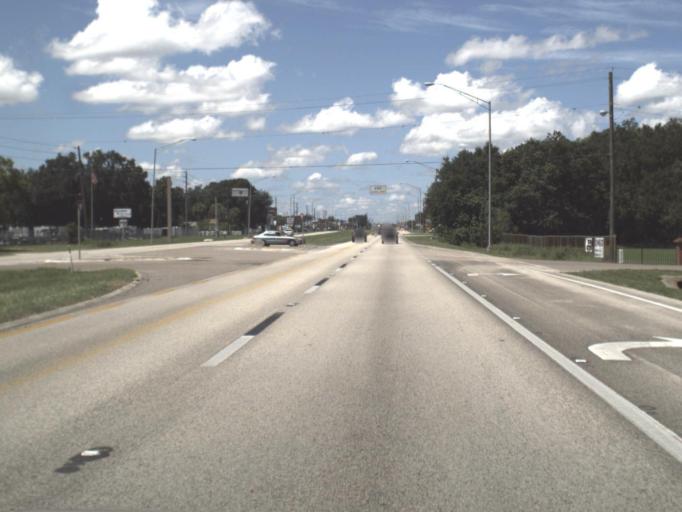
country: US
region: Florida
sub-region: Polk County
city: Combee Settlement
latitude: 28.0480
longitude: -81.8997
